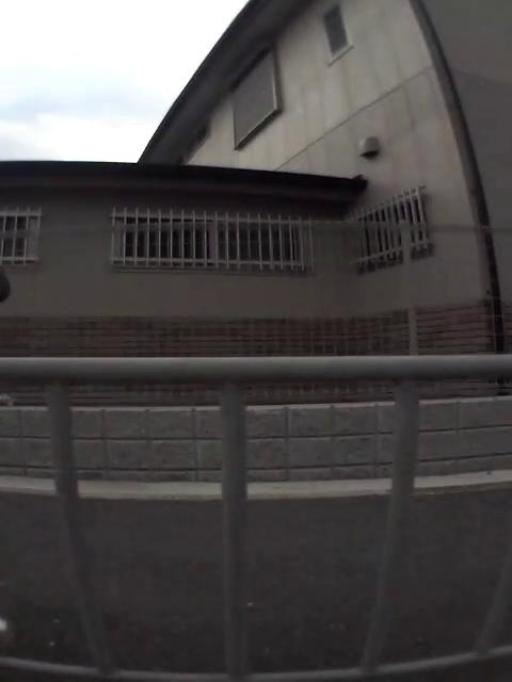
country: JP
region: Osaka
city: Neyagawa
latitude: 34.7472
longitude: 135.6228
